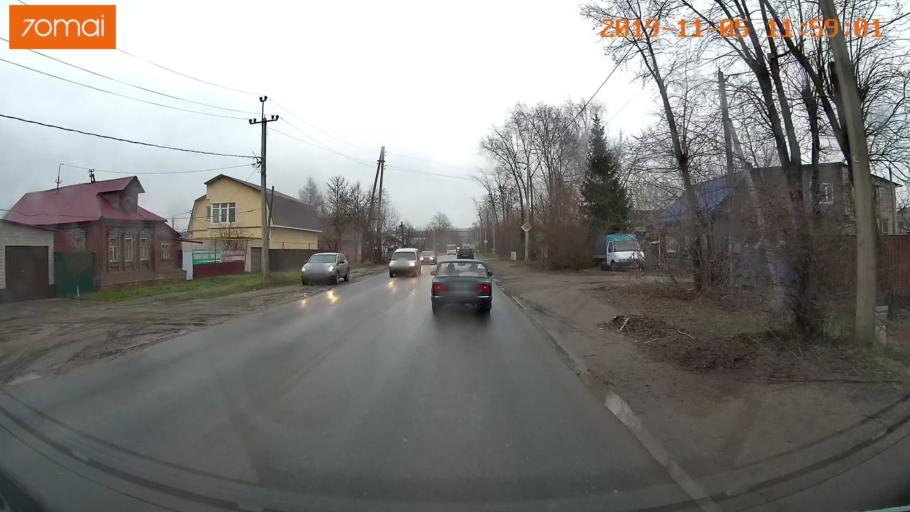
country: RU
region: Ivanovo
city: Kokhma
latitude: 56.9795
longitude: 41.0446
